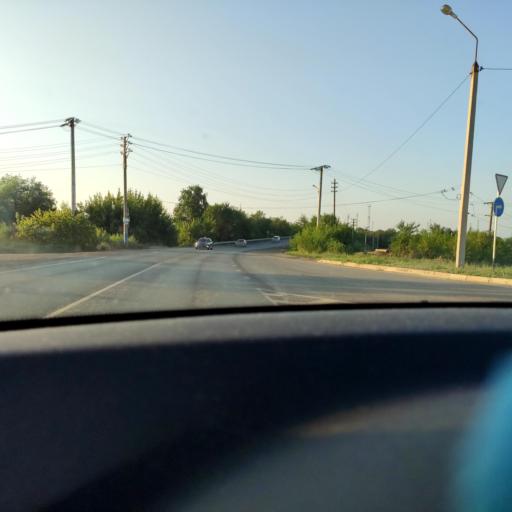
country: RU
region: Samara
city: Kinel'
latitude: 53.2388
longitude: 50.5803
